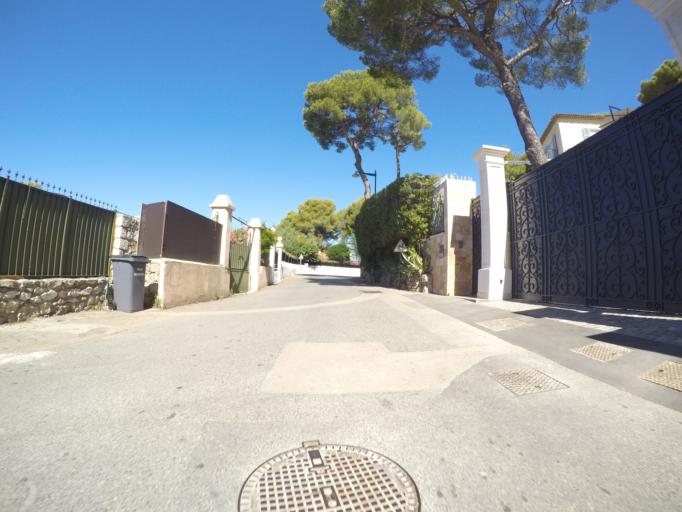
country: FR
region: Provence-Alpes-Cote d'Azur
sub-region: Departement des Alpes-Maritimes
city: Saint-Jean-Cap-Ferrat
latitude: 43.6856
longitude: 7.3250
